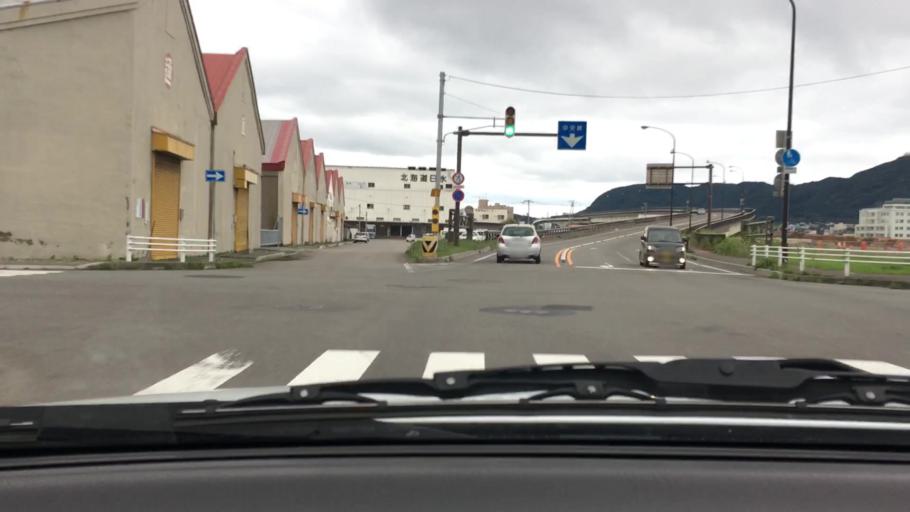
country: JP
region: Hokkaido
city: Hakodate
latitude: 41.7866
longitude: 140.7281
